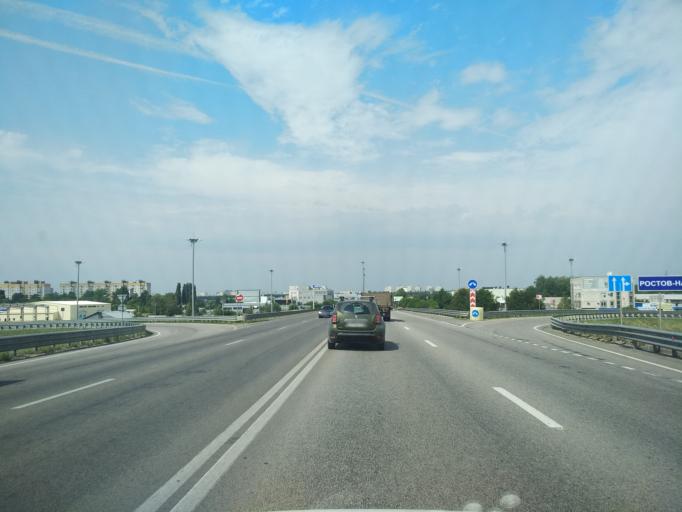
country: RU
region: Voronezj
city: Somovo
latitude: 51.6780
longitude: 39.3006
